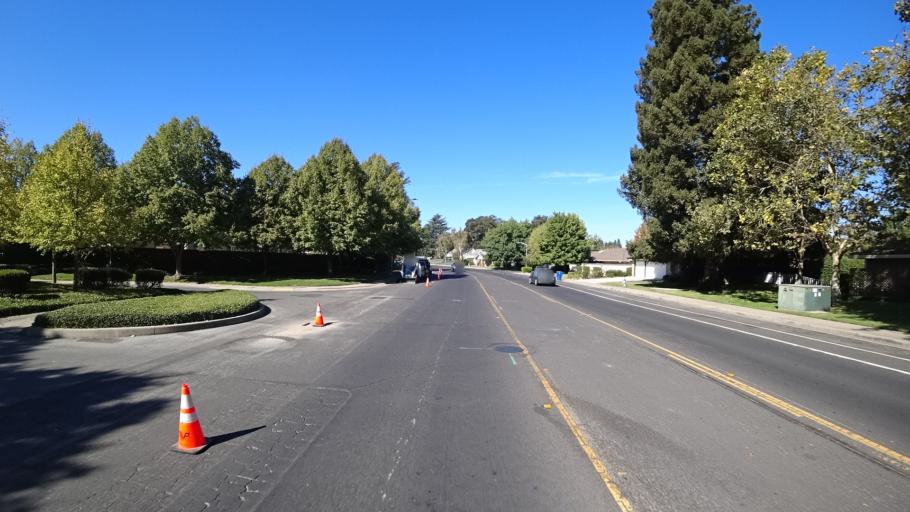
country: US
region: California
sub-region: Sacramento County
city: Parkway
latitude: 38.4835
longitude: -121.5221
